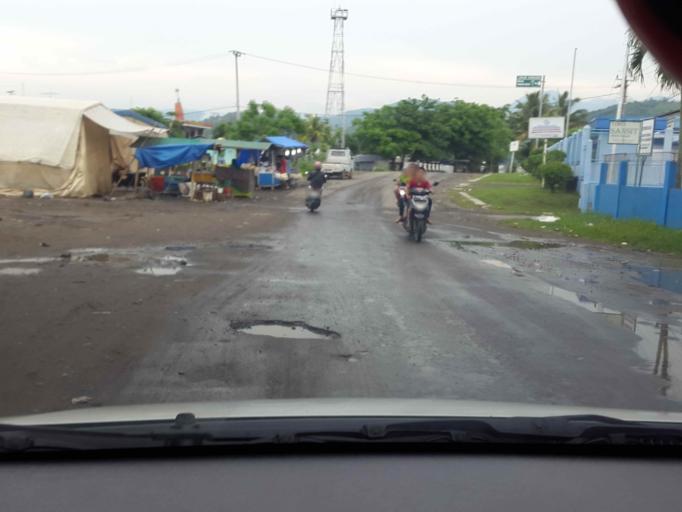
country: ID
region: West Java
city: Pelabuhanratu
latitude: -6.9922
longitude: 106.5432
